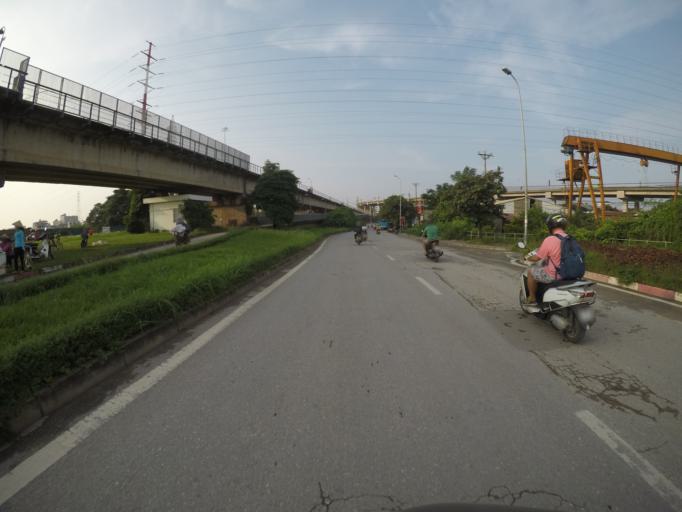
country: VN
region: Ha Noi
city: Tay Ho
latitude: 21.0863
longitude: 105.7858
